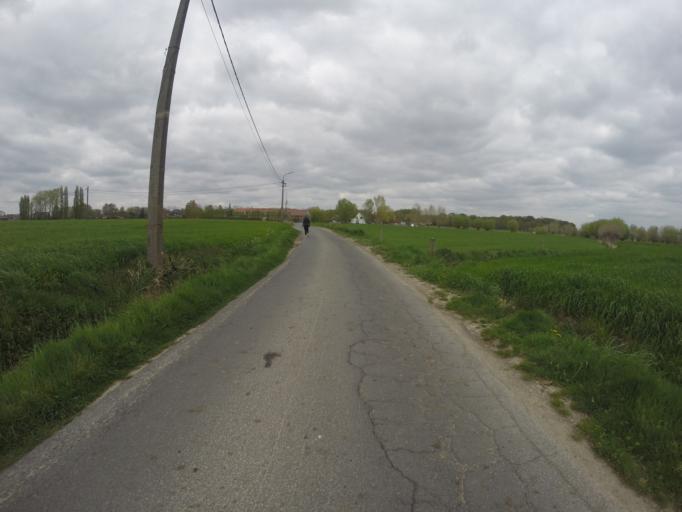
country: BE
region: Flanders
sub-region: Provincie West-Vlaanderen
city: Ruiselede
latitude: 51.0358
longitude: 3.4480
